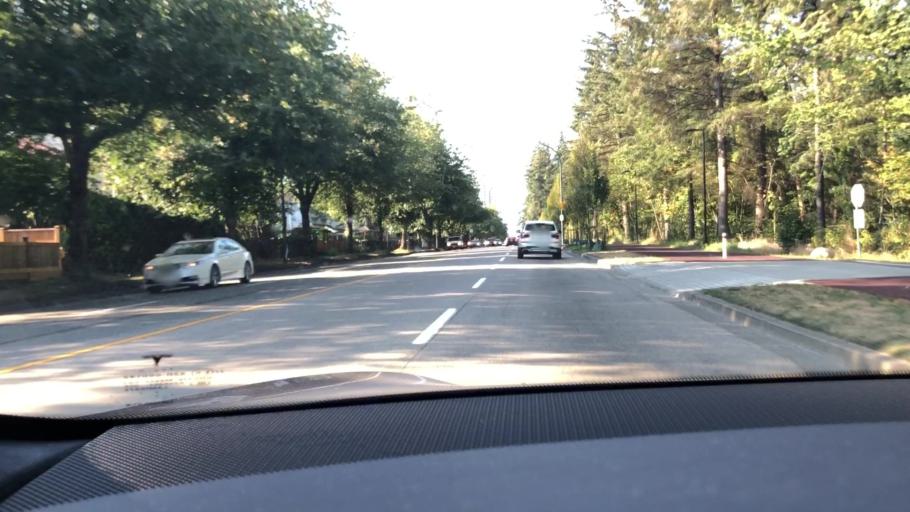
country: CA
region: British Columbia
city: Burnaby
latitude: 49.2266
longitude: -123.0235
